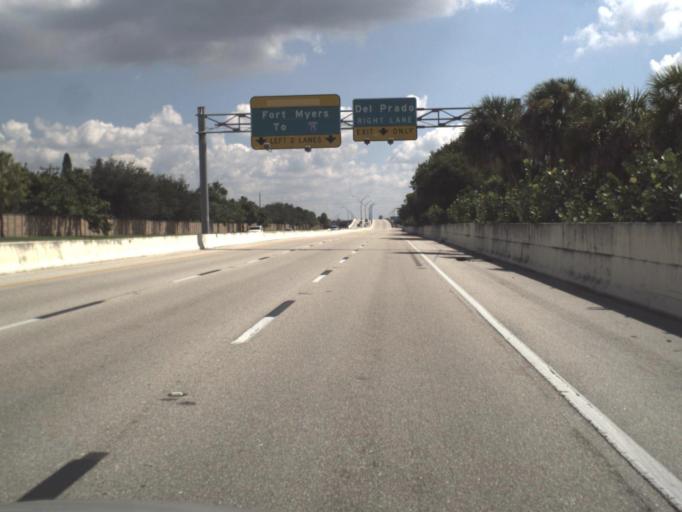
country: US
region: Florida
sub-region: Lee County
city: Cape Coral
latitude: 26.6073
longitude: -81.9495
